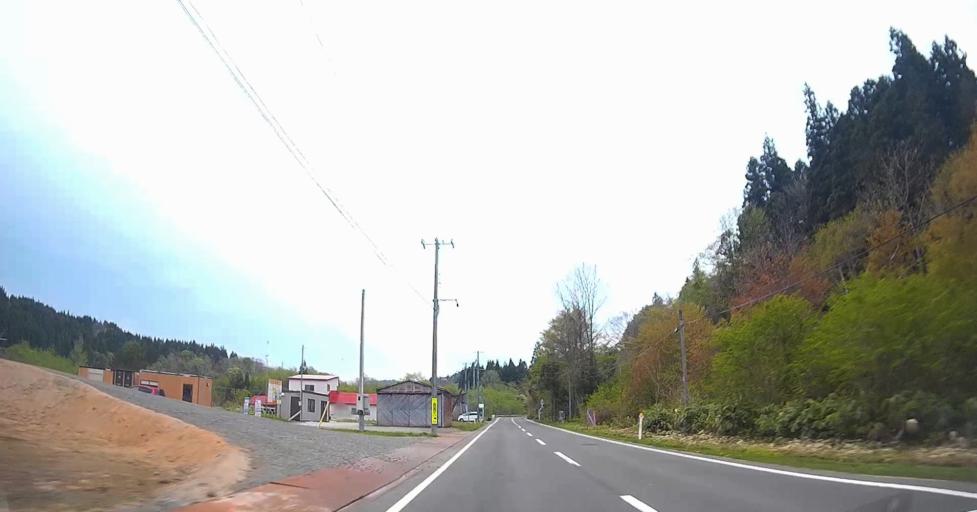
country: JP
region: Aomori
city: Goshogawara
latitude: 41.1296
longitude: 140.5198
